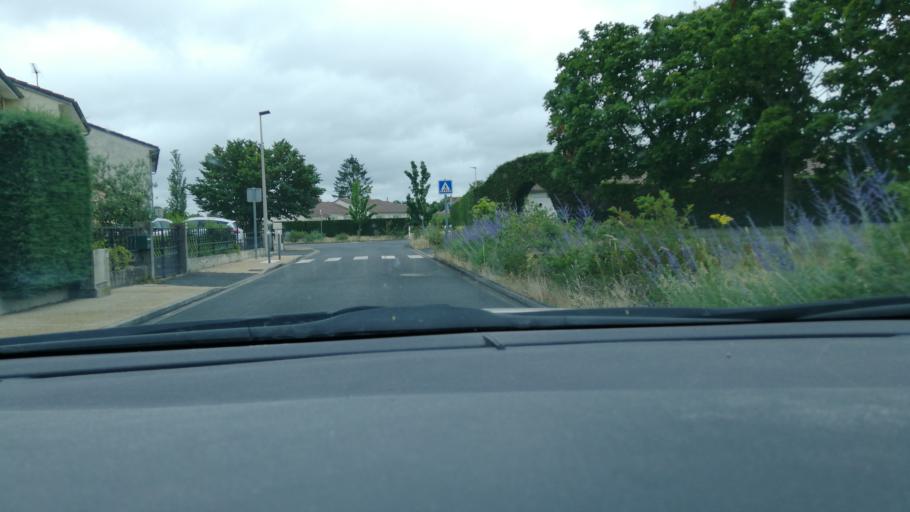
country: FR
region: Poitou-Charentes
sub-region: Departement de la Vienne
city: Antran
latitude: 46.8779
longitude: 0.5689
